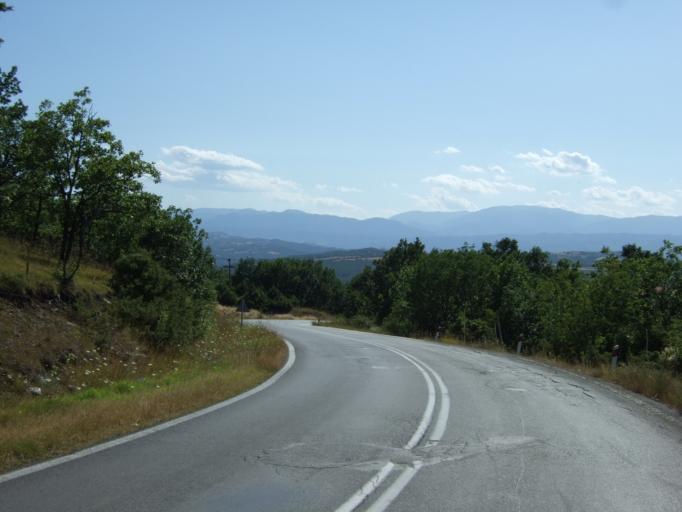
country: GR
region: West Macedonia
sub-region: Nomos Grevenon
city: Grevena
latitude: 39.9803
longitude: 21.5134
